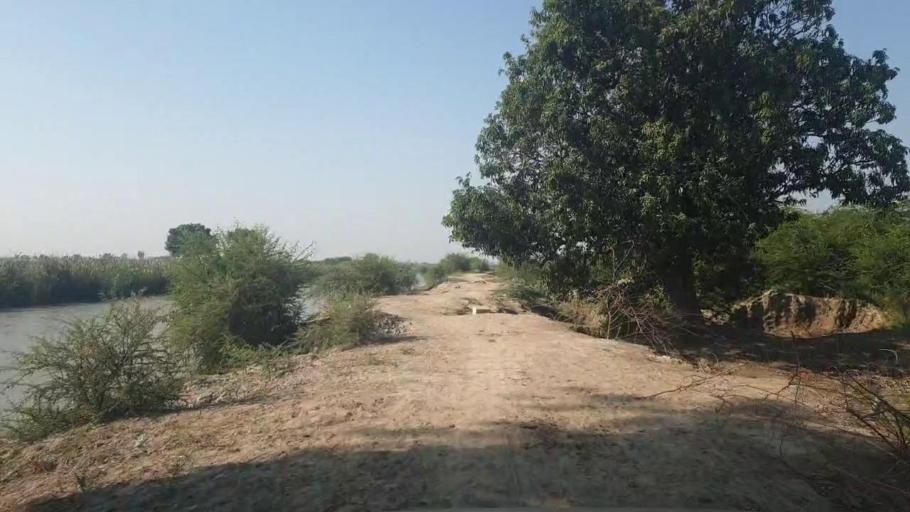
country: PK
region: Sindh
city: Badin
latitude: 24.6980
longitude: 68.8763
